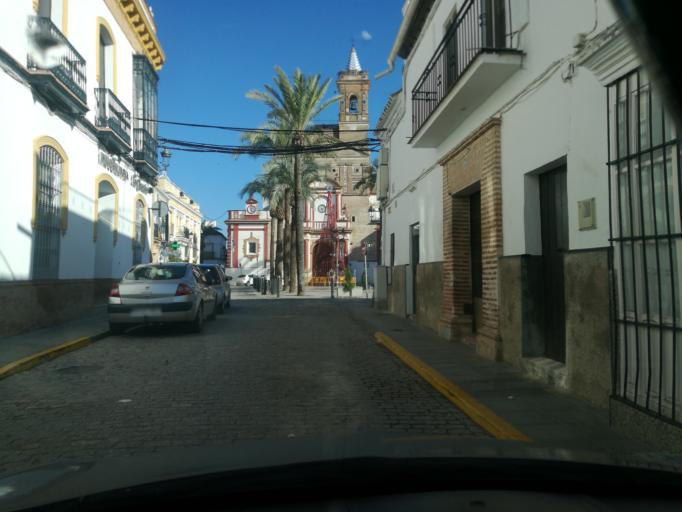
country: ES
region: Andalusia
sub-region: Provincia de Sevilla
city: La Campana
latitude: 37.5695
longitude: -5.4268
